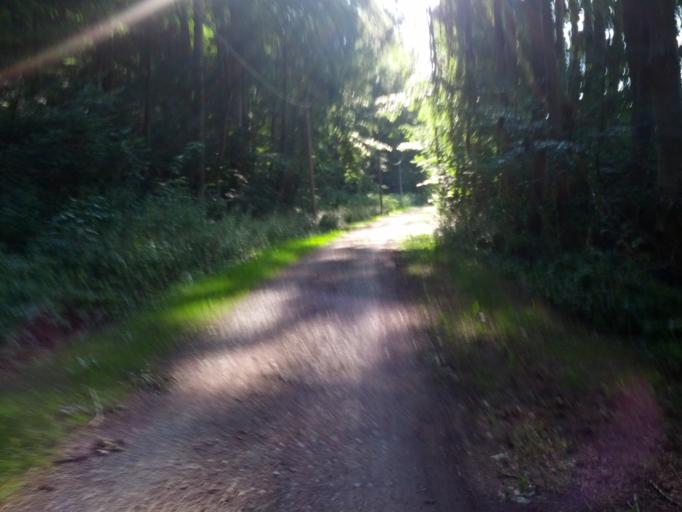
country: DE
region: Thuringia
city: Ebenshausen
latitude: 51.0714
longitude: 10.2914
